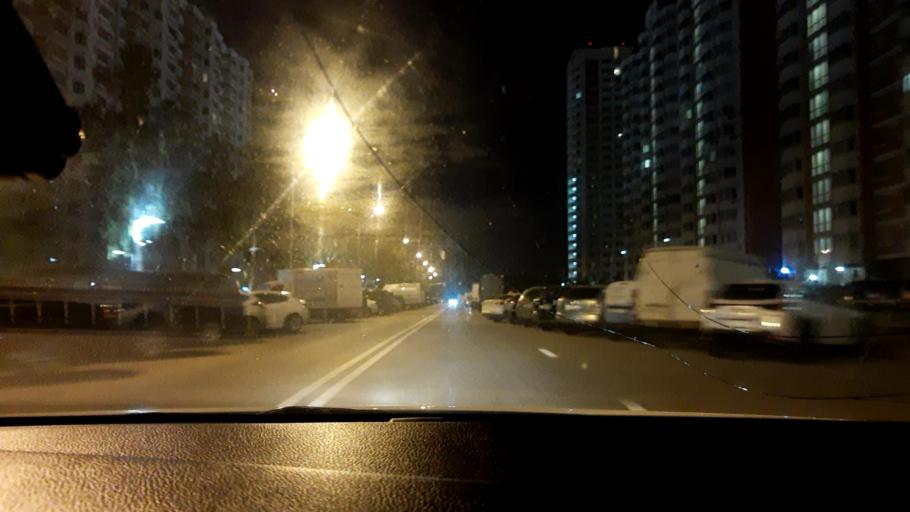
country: RU
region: Moskovskaya
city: Moskovskiy
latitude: 55.6029
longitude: 37.3632
